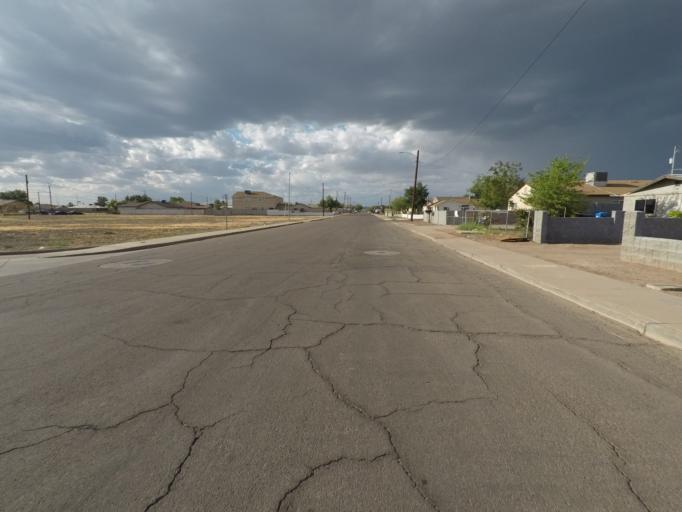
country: US
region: Arizona
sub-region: Maricopa County
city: Phoenix
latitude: 33.4345
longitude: -112.0890
